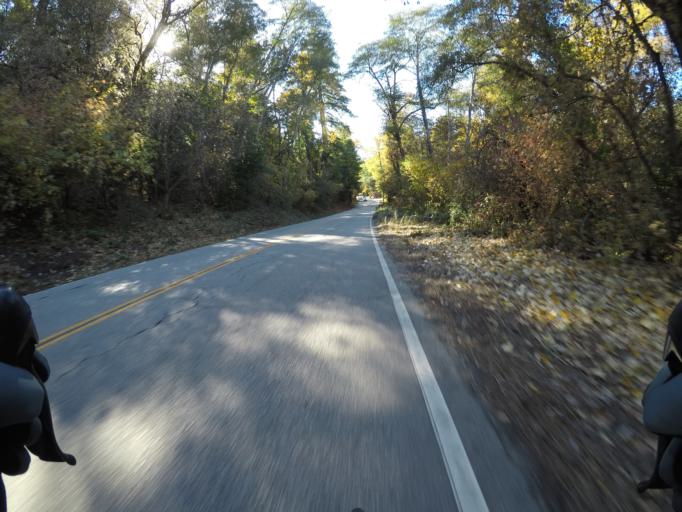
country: US
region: California
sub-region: Santa Cruz County
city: Mount Hermon
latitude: 37.0612
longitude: -122.0566
